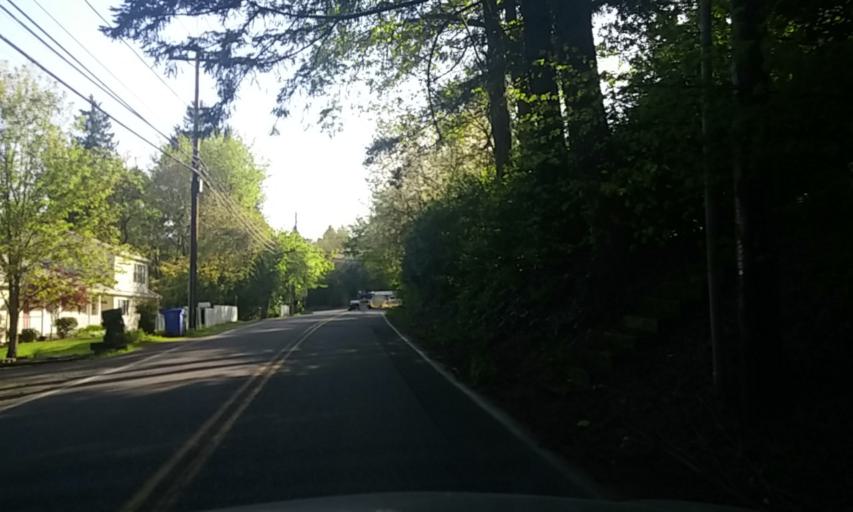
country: US
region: Oregon
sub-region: Washington County
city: Metzger
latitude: 45.4400
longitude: -122.7395
